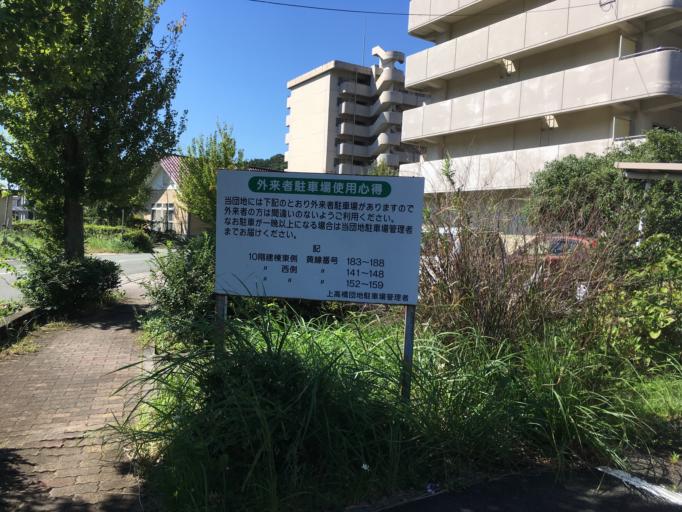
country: JP
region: Kumamoto
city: Kumamoto
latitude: 32.7875
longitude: 130.6642
